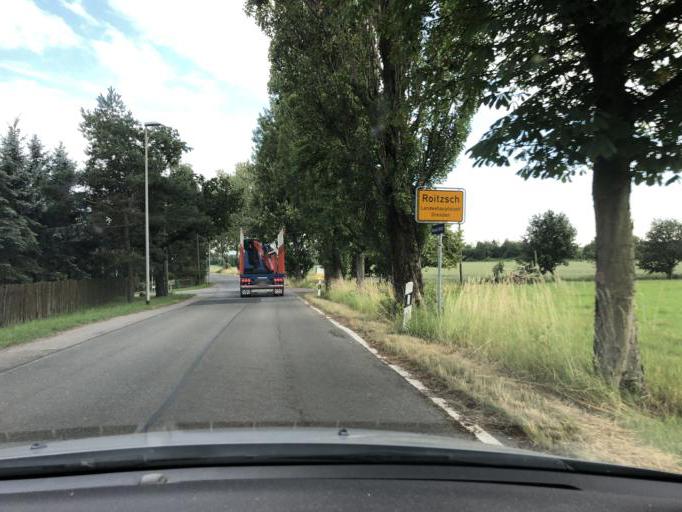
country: DE
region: Saxony
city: Freital
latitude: 51.0547
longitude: 13.6070
